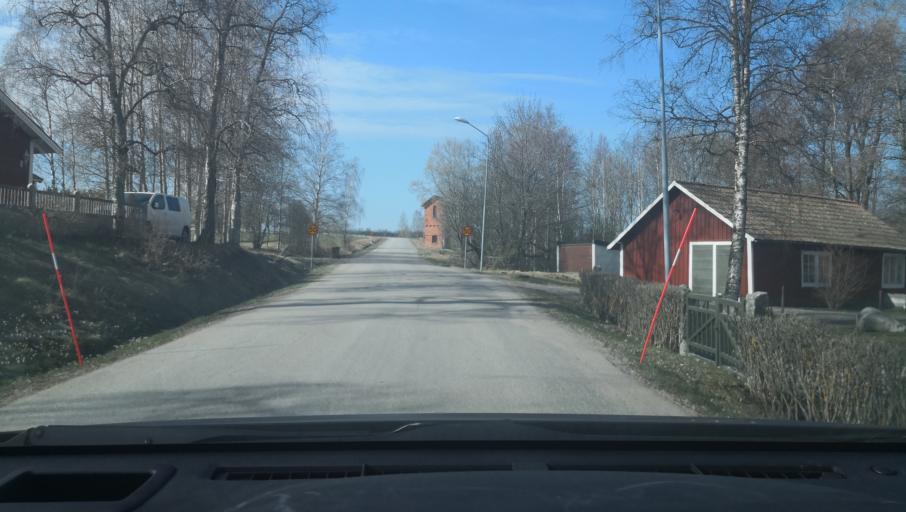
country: SE
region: Uppsala
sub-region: Heby Kommun
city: Morgongava
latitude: 59.8424
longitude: 16.9156
